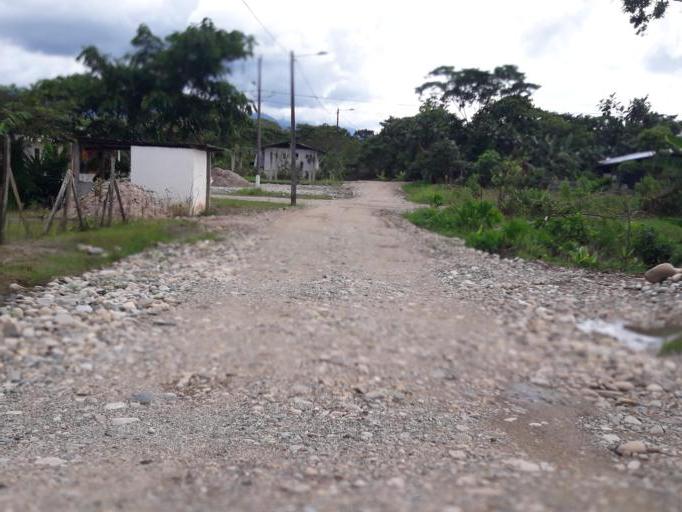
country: EC
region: Napo
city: Tena
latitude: -0.9547
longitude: -77.8170
